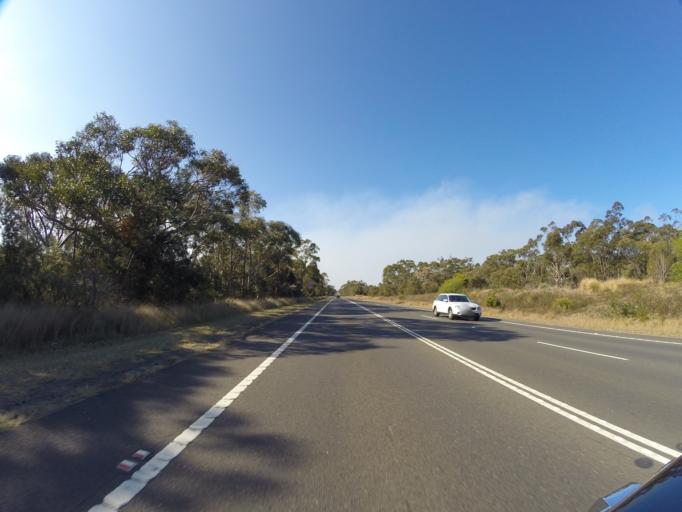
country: AU
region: New South Wales
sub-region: Liverpool
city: Holsworthy
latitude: -34.0278
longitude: 150.9657
